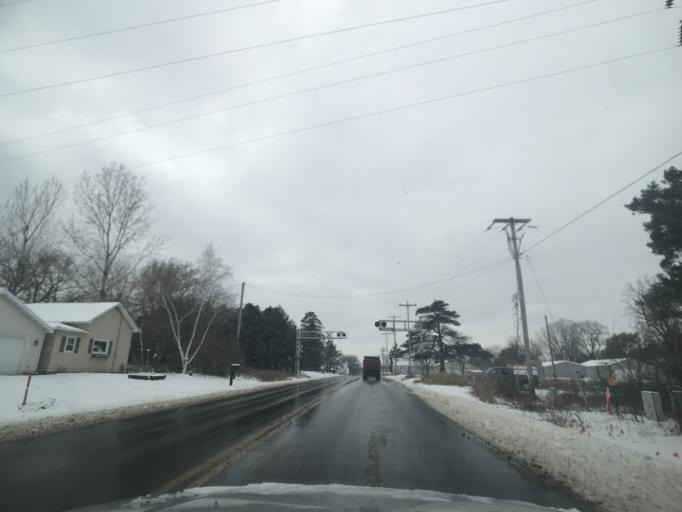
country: US
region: Wisconsin
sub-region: Brown County
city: Suamico
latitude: 44.7209
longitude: -88.0661
